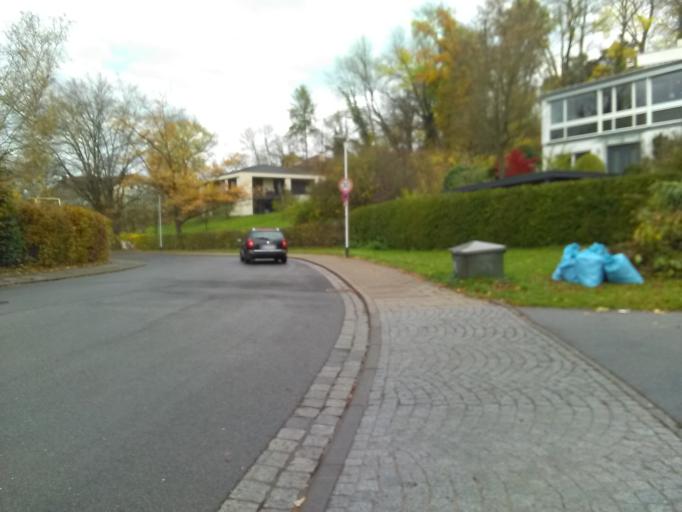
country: DE
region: Bavaria
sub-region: Upper Franconia
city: Bamberg
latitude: 49.8840
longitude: 10.8803
